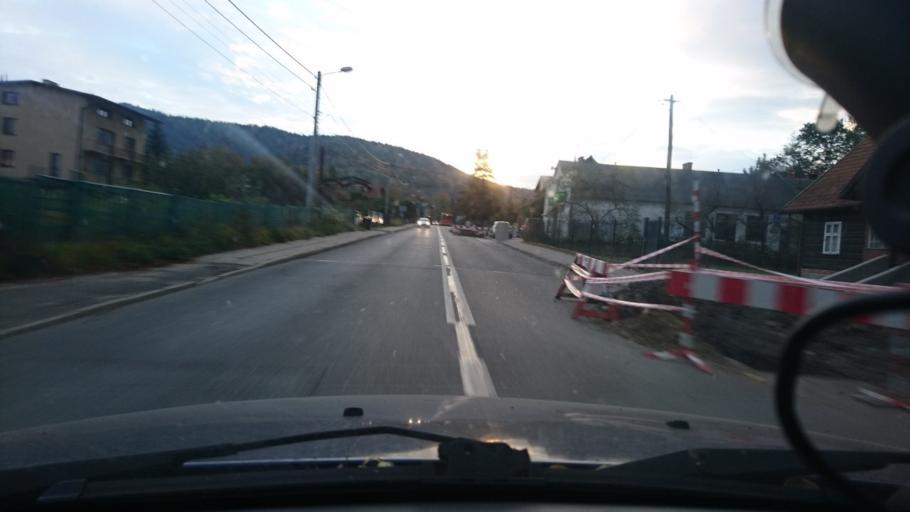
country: PL
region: Silesian Voivodeship
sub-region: Powiat bielski
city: Wilkowice
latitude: 49.8015
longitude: 19.0840
